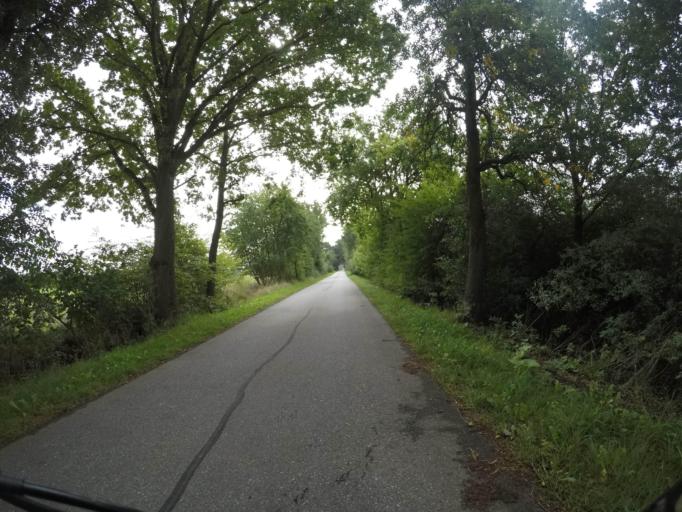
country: DE
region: Lower Saxony
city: Neu Darchau
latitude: 53.3004
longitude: 10.8577
